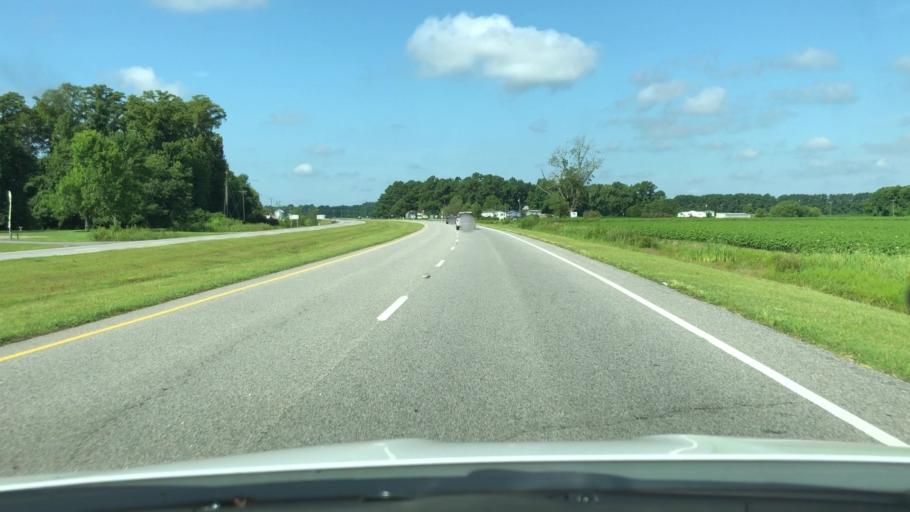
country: US
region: North Carolina
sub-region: Chowan County
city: Edenton
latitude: 36.0972
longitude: -76.5412
